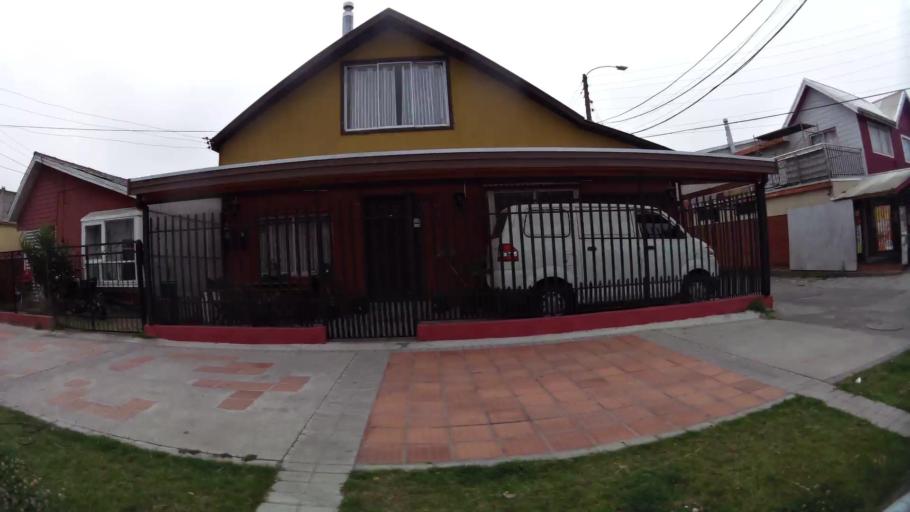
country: CL
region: Biobio
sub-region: Provincia de Concepcion
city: Concepcion
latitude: -36.7945
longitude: -73.0813
